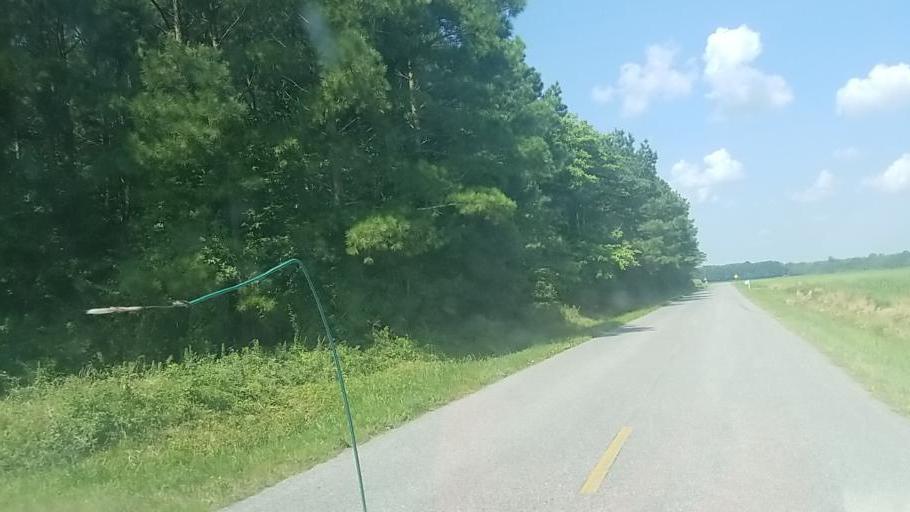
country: US
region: Maryland
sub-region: Worcester County
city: Berlin
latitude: 38.2972
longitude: -75.2672
